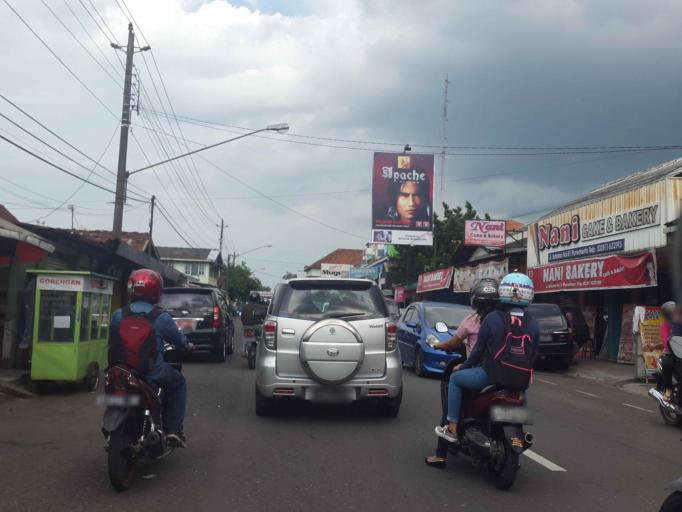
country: ID
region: Central Java
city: Purwokerto
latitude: -7.4171
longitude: 109.2460
